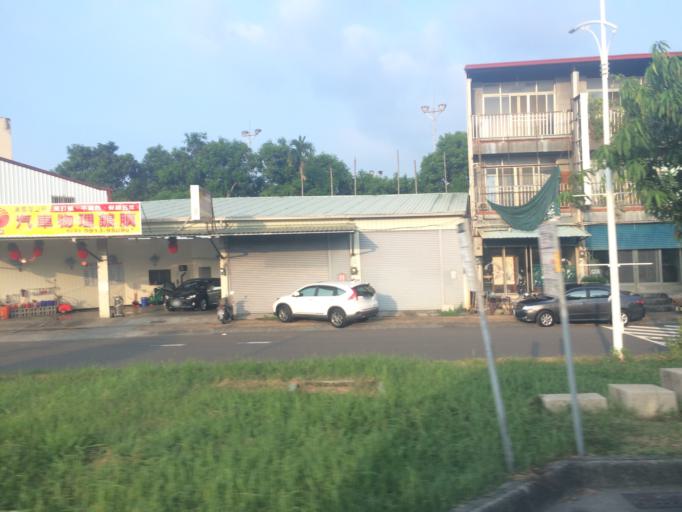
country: TW
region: Taiwan
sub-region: Chiayi
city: Jiayi Shi
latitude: 23.5093
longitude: 120.4462
